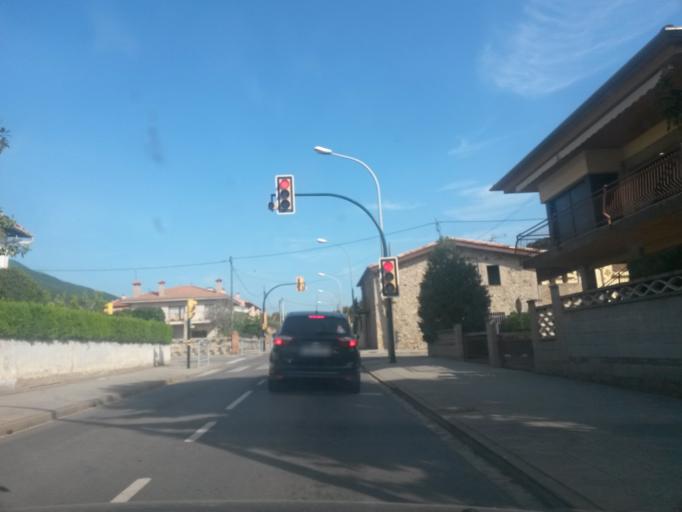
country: ES
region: Catalonia
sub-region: Provincia de Girona
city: les Planes d'Hostoles
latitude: 42.0579
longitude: 2.5389
